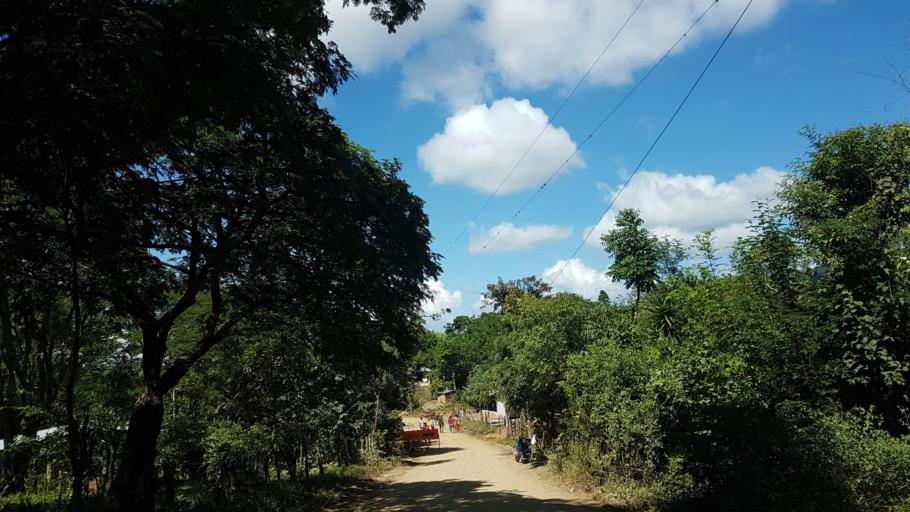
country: HN
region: El Paraiso
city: Santa Cruz
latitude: 13.7322
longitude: -86.6855
